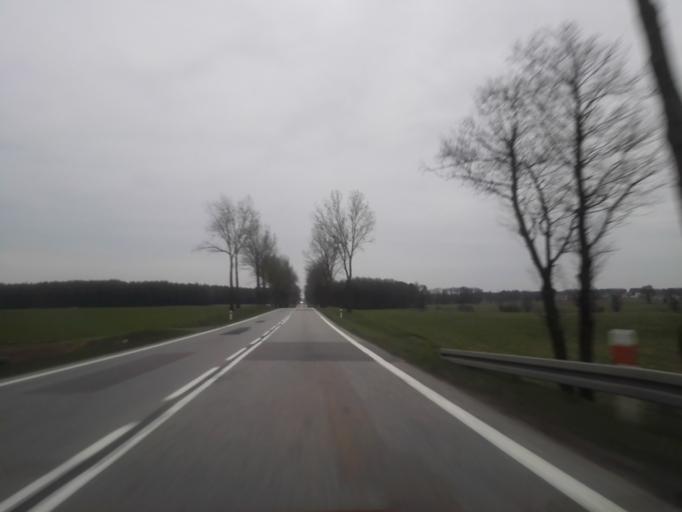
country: PL
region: Podlasie
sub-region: Powiat kolnenski
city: Stawiski
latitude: 53.3169
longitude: 22.1514
